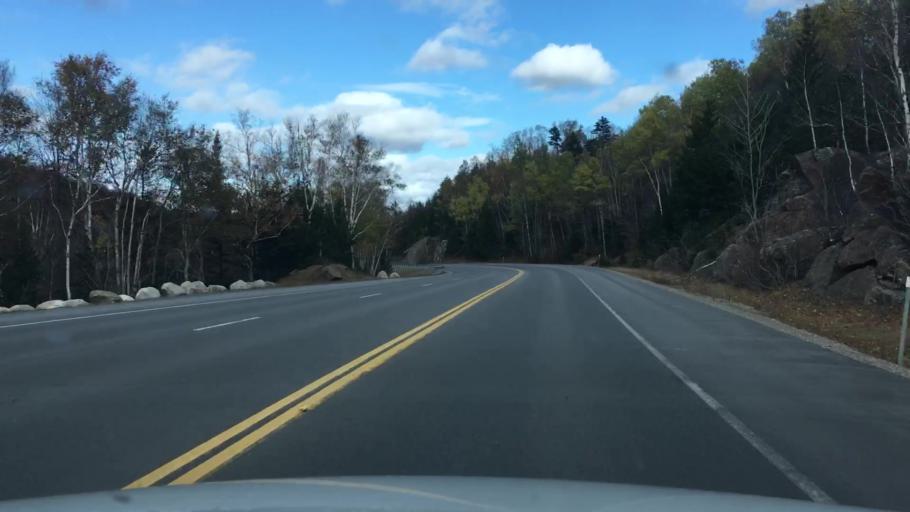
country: US
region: New Hampshire
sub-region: Coos County
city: Gorham
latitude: 44.2803
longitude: -71.2315
